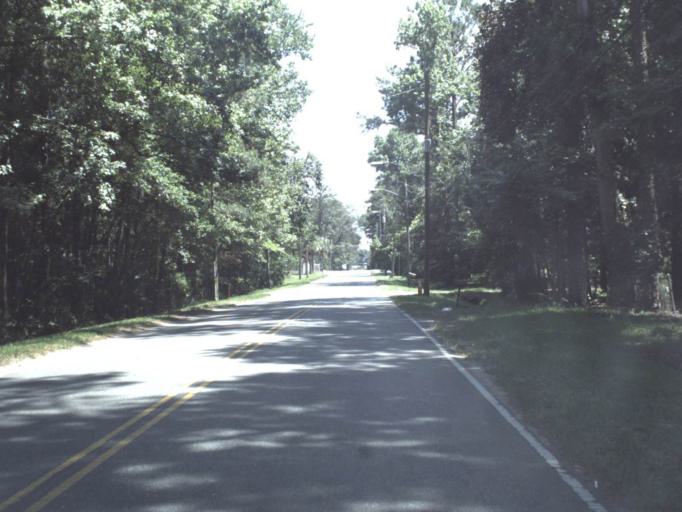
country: US
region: Florida
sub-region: Duval County
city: Jacksonville
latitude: 30.3687
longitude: -81.7341
